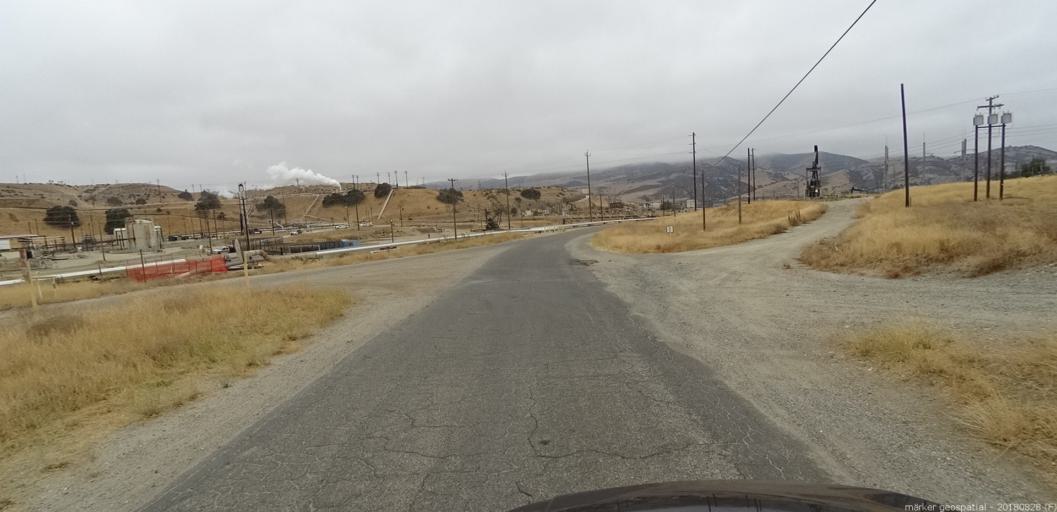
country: US
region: California
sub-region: San Luis Obispo County
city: Lake Nacimiento
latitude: 35.9536
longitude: -120.8528
